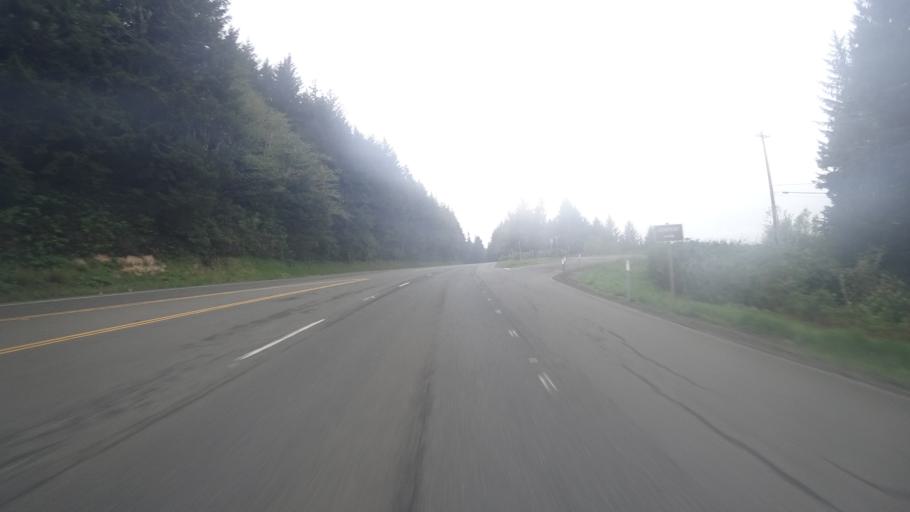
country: US
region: Oregon
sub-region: Coos County
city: Lakeside
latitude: 43.6589
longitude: -124.1880
